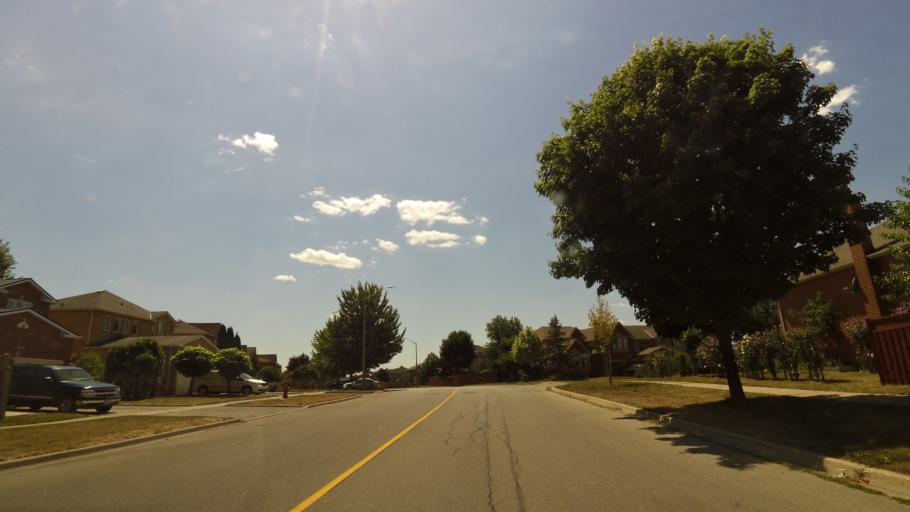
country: CA
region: Ontario
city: Brampton
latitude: 43.6424
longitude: -79.8715
